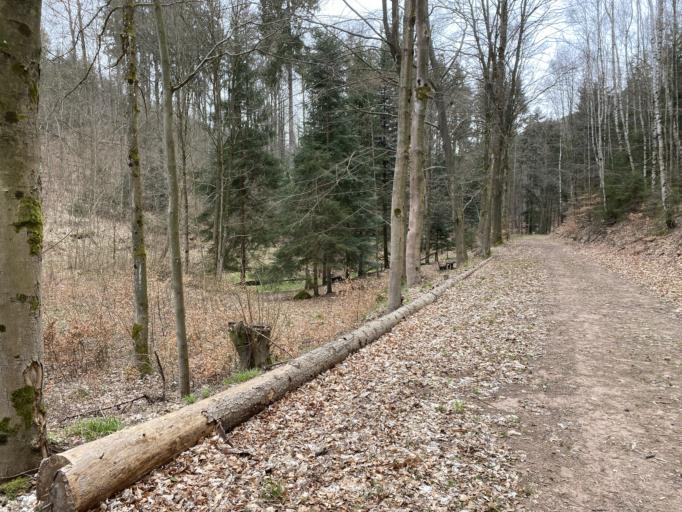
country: DE
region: Rheinland-Pfalz
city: Neidenfels
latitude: 49.4145
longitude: 8.0512
